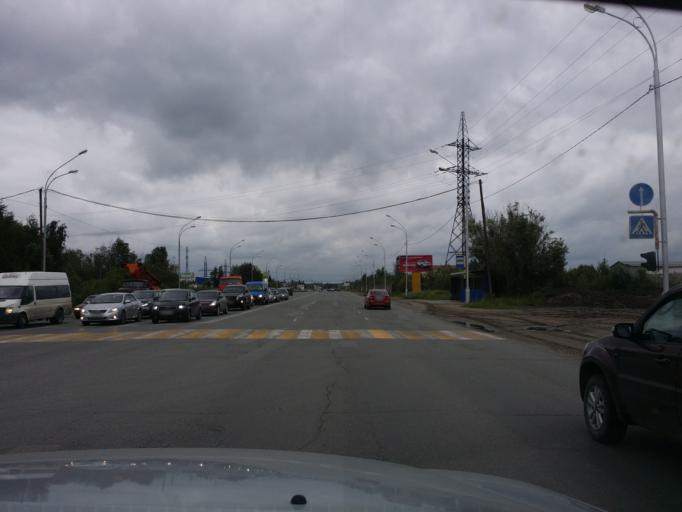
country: RU
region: Khanty-Mansiyskiy Avtonomnyy Okrug
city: Nizhnevartovsk
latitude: 60.9554
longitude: 76.5302
